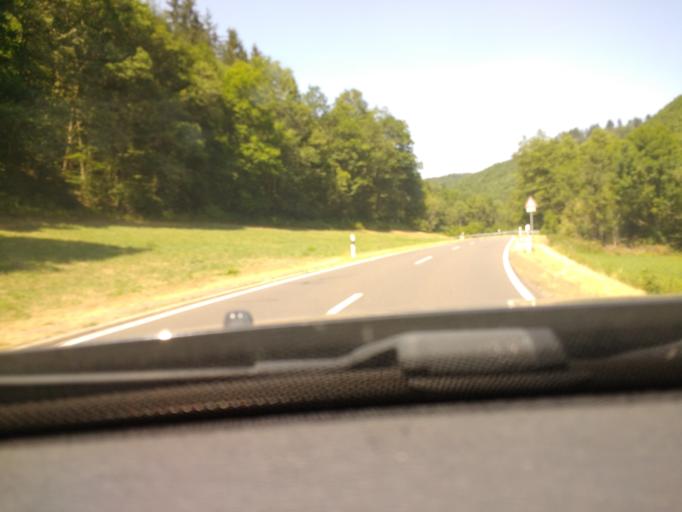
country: DE
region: Rheinland-Pfalz
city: Bettenfeld
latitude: 50.0982
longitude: 6.7853
